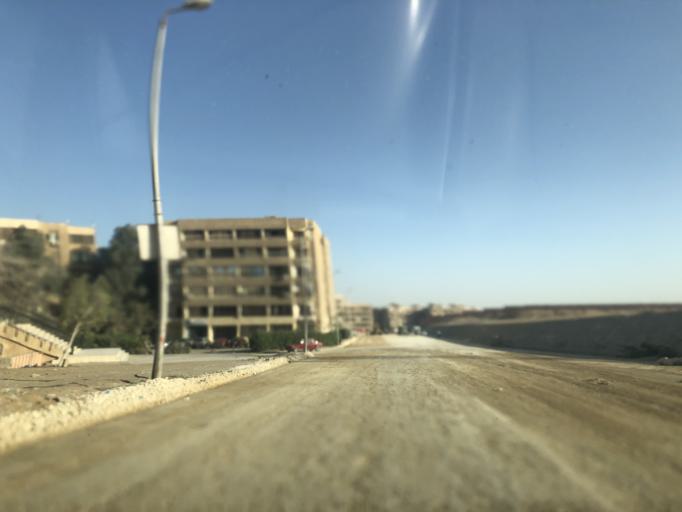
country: EG
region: Al Jizah
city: Al Jizah
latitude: 29.9886
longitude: 31.1116
